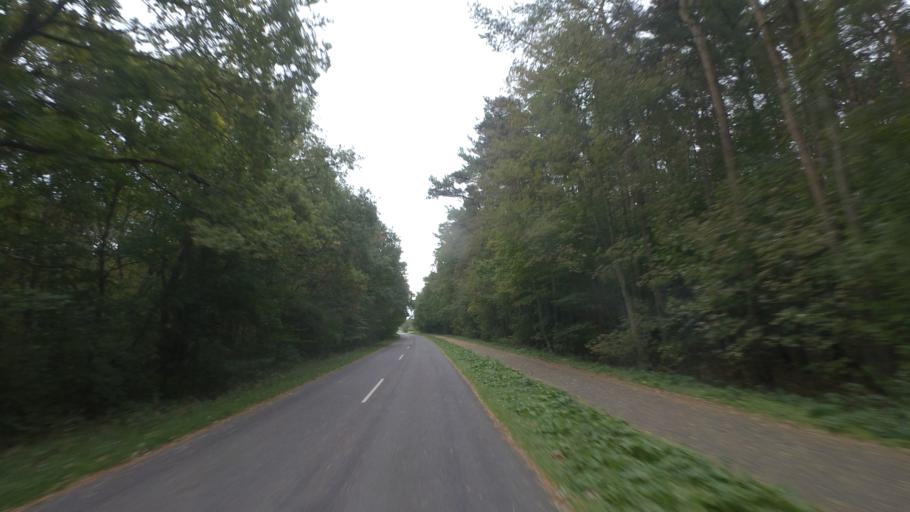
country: DK
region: Capital Region
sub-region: Bornholm Kommune
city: Nexo
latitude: 55.0031
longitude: 15.0423
